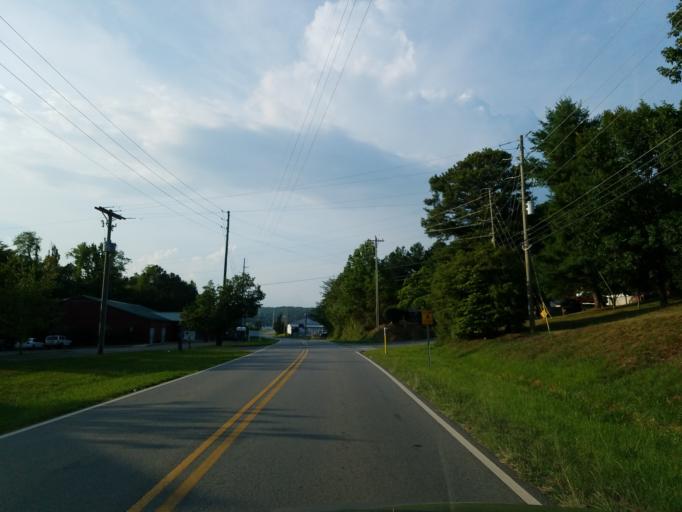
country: US
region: Georgia
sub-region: Gilmer County
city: Ellijay
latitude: 34.6761
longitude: -84.4895
